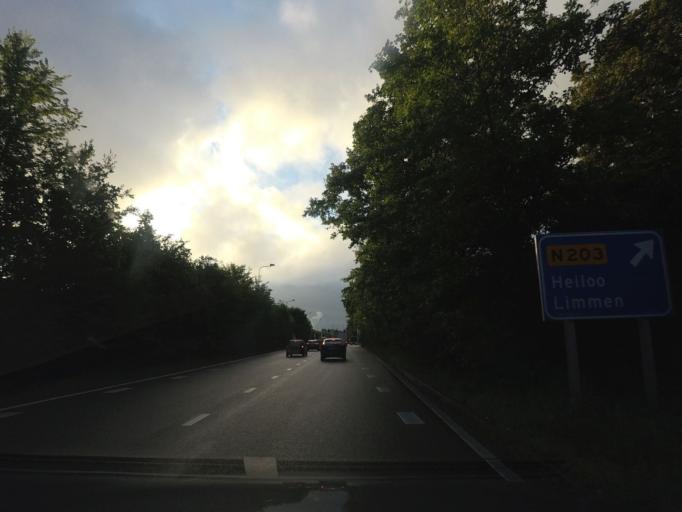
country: NL
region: North Holland
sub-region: Gemeente Alkmaar
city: Alkmaar
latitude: 52.6198
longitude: 4.7290
